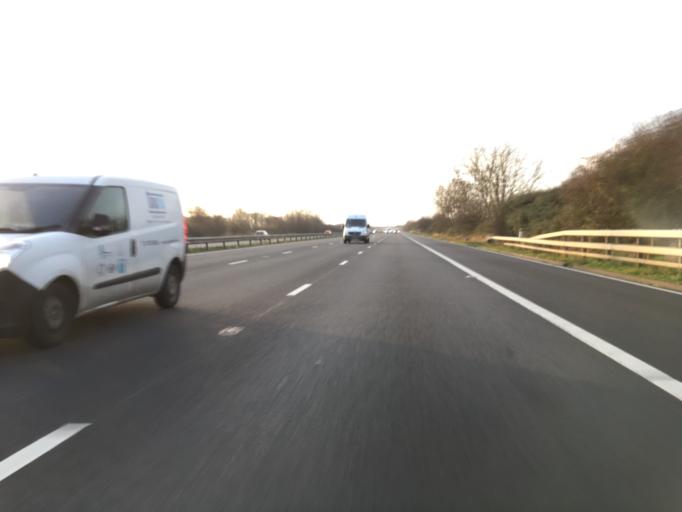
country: GB
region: England
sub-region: Gloucestershire
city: Tewkesbury
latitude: 51.9817
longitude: -2.1263
